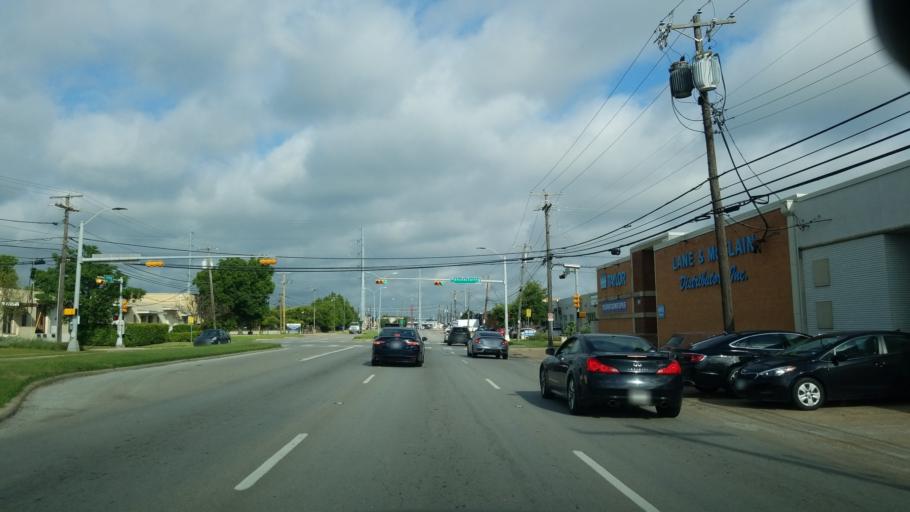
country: US
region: Texas
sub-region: Dallas County
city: Dallas
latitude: 32.7954
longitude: -96.8297
